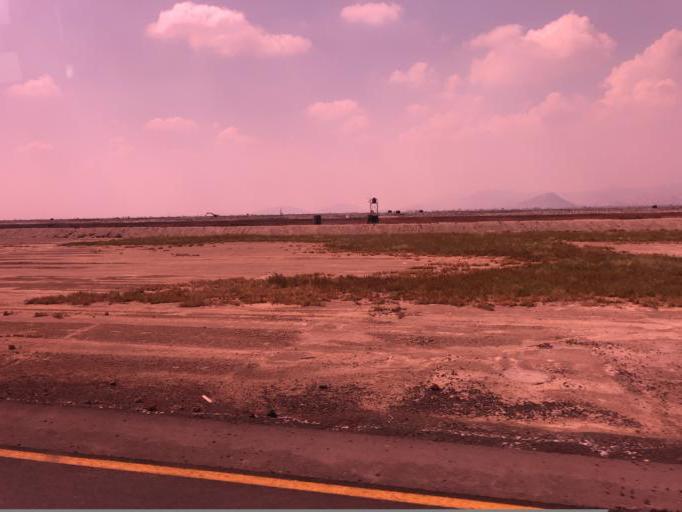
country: MX
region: Mexico
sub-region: Atenco
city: Colonia el Salado
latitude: 19.5383
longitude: -98.9852
